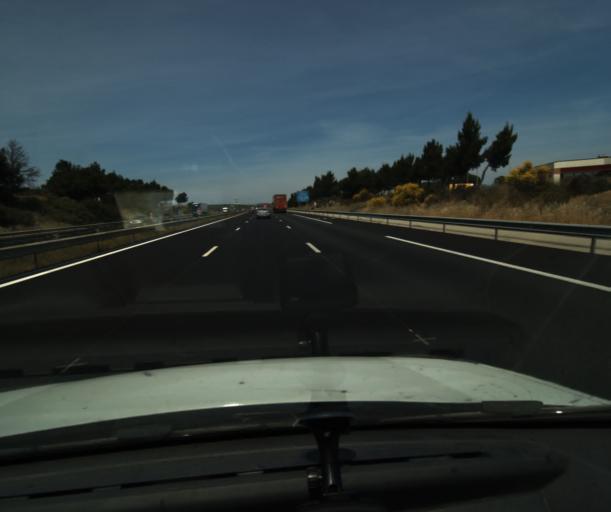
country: FR
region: Languedoc-Roussillon
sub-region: Departement de l'Aude
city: Leucate
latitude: 42.9499
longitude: 2.9710
